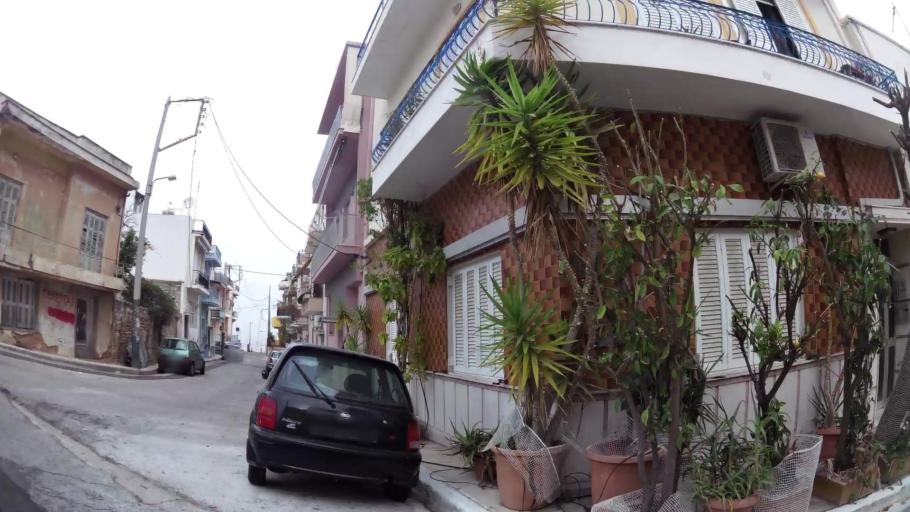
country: GR
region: Attica
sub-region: Nomos Attikis
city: Piraeus
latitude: 37.9409
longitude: 23.6572
